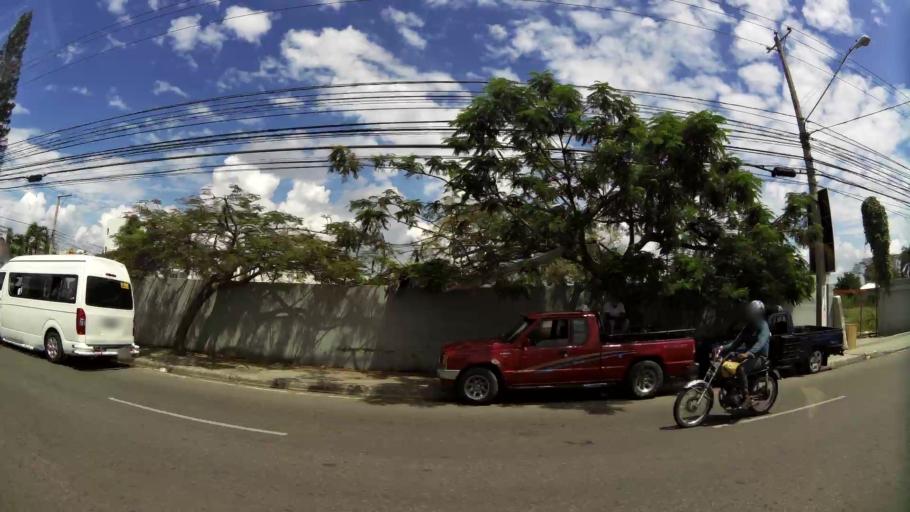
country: DO
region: Santiago
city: Santiago de los Caballeros
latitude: 19.4561
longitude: -70.6648
